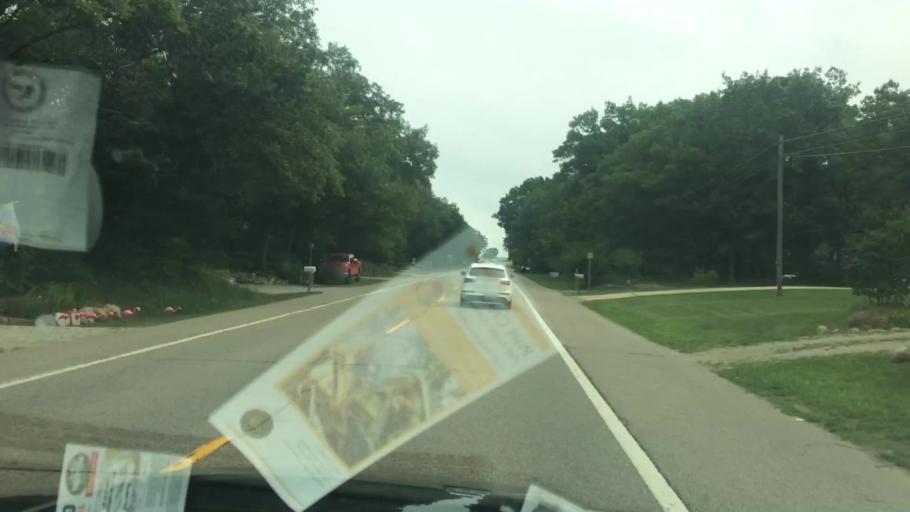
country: US
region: Michigan
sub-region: Huron County
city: Pigeon
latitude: 43.9840
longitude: -83.1711
